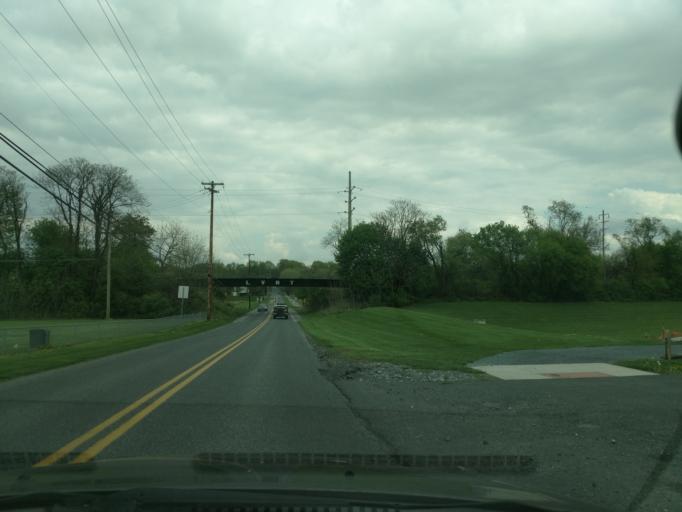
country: US
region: Pennsylvania
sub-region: Lebanon County
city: Lebanon South
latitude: 40.3225
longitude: -76.4170
